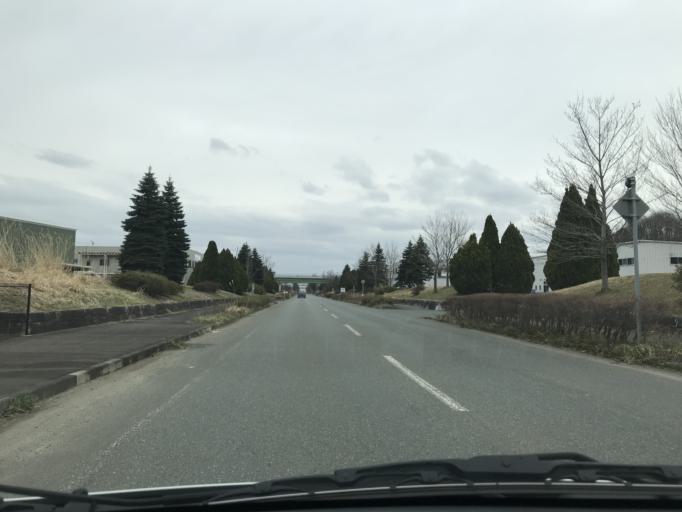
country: JP
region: Iwate
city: Kitakami
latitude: 39.2605
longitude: 141.1092
